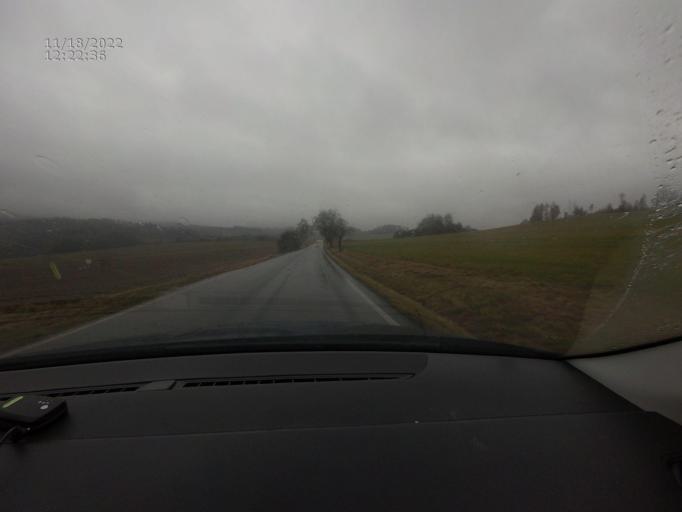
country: CZ
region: Plzensky
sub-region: Okres Plzen-Jih
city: Nepomuk
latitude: 49.4547
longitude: 13.5418
